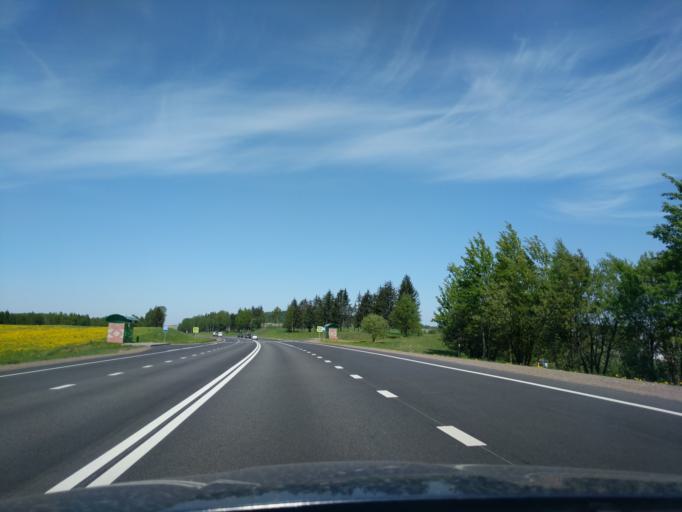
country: BY
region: Minsk
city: Bal'shavik
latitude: 54.0856
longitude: 27.5519
